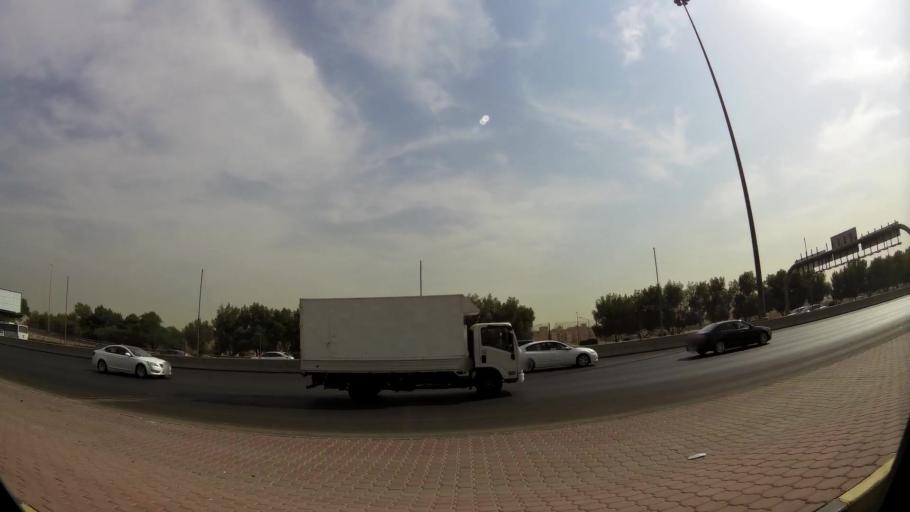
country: KW
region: Al Farwaniyah
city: Janub as Surrah
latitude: 29.2814
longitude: 47.9856
